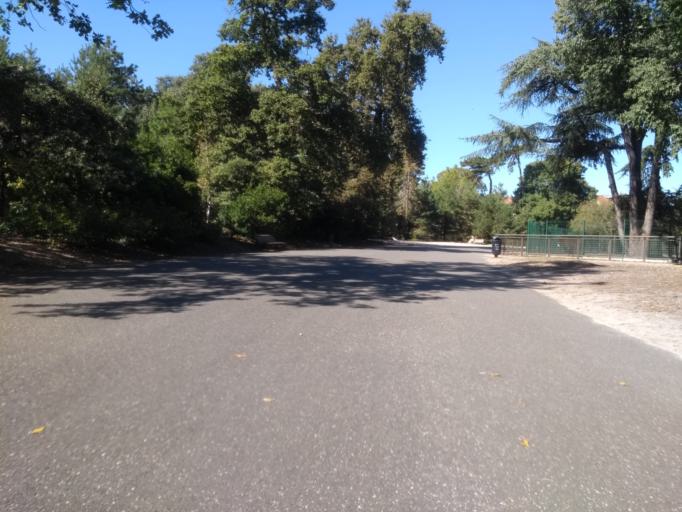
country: FR
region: Aquitaine
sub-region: Departement de la Gironde
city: Le Bouscat
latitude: 44.8512
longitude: -0.6041
